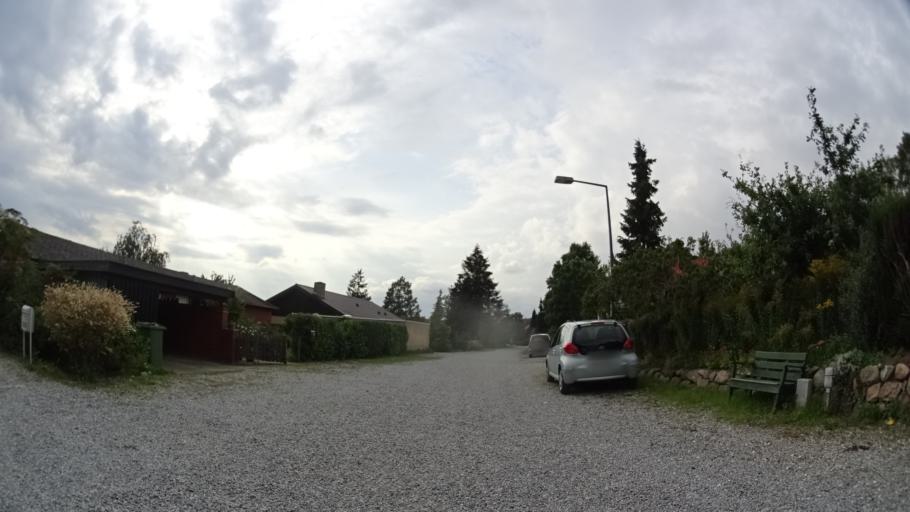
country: DK
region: Central Jutland
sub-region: Arhus Kommune
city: Stavtrup
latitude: 56.1520
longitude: 10.1223
